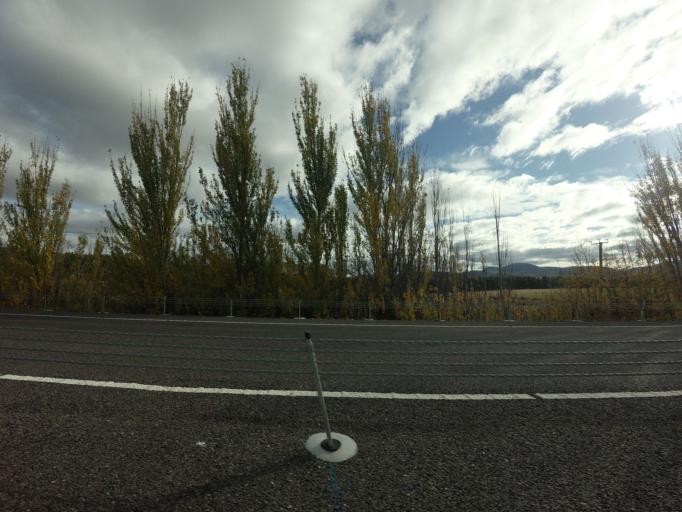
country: AU
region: Tasmania
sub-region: Brighton
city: Bridgewater
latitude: -42.5066
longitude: 147.1882
